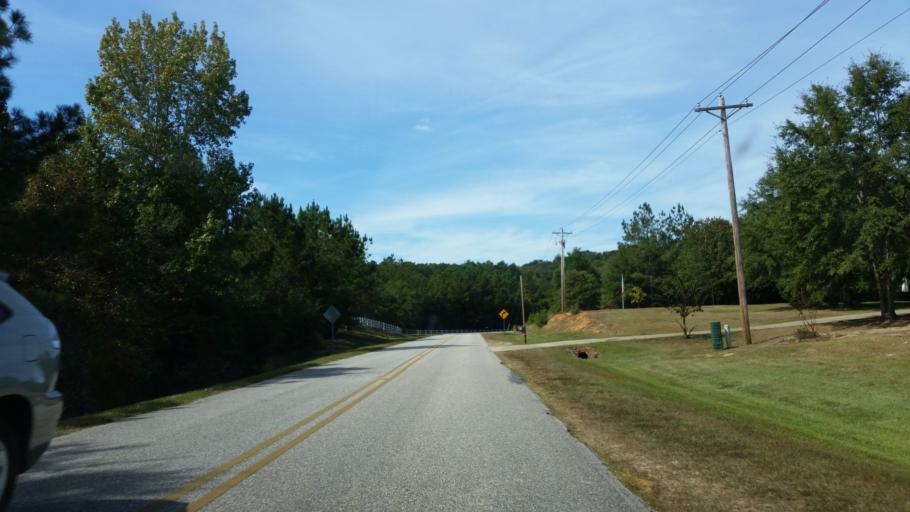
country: US
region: Alabama
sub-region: Baldwin County
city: Spanish Fort
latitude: 30.7425
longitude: -87.8878
